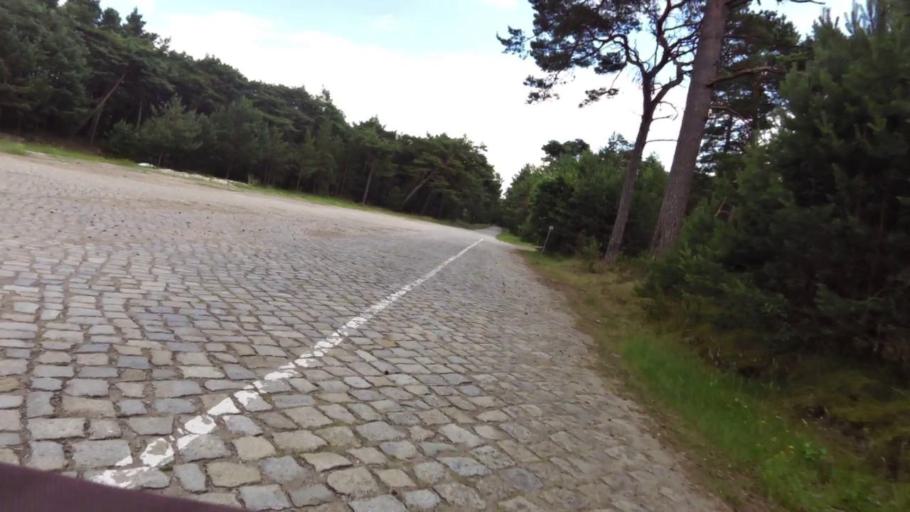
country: PL
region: West Pomeranian Voivodeship
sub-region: Powiat gryficki
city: Mrzezyno
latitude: 54.1269
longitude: 15.2199
